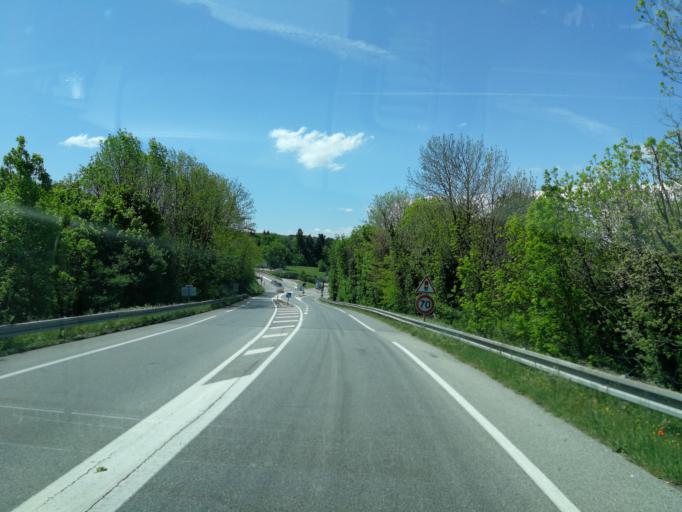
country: FR
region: Rhone-Alpes
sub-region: Departement de la Drome
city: Crest
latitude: 44.7230
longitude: 5.0179
